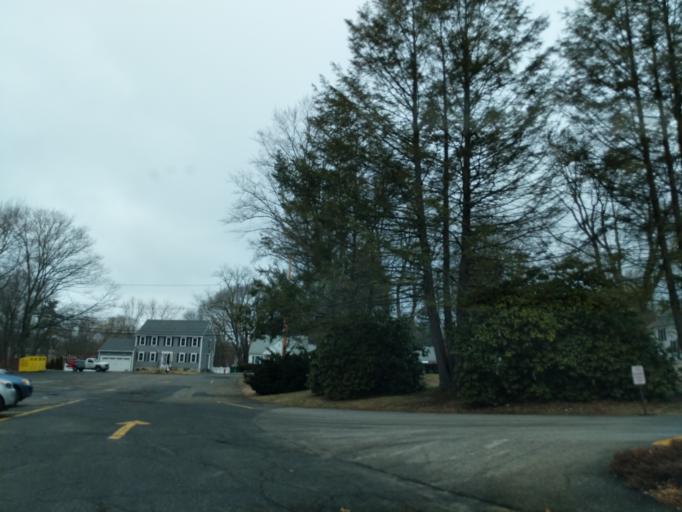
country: US
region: Massachusetts
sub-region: Middlesex County
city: Natick
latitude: 42.2798
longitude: -71.3753
